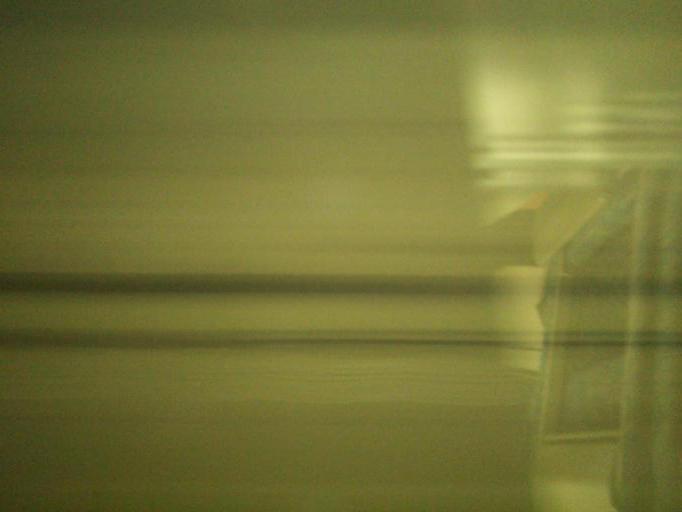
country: JP
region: Kochi
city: Nakamura
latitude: 33.0636
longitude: 133.1062
